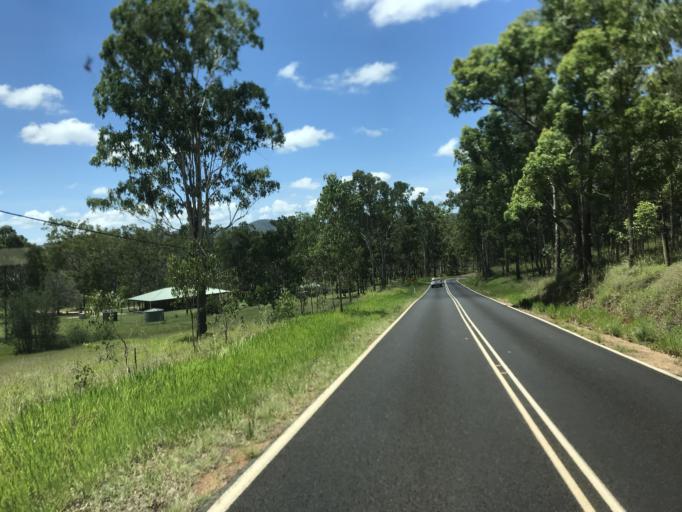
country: AU
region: Queensland
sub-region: Tablelands
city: Atherton
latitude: -17.4204
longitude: 145.3937
